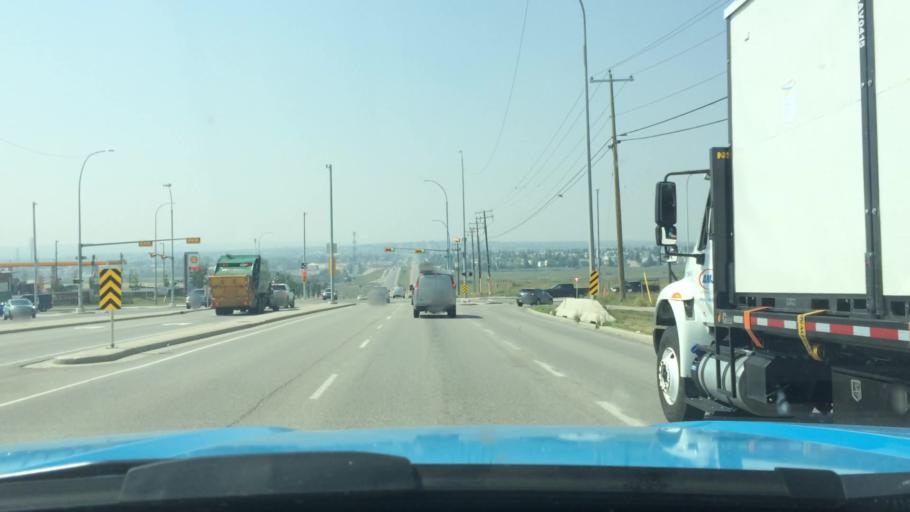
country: CA
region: Alberta
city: Calgary
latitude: 51.1538
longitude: -114.0266
